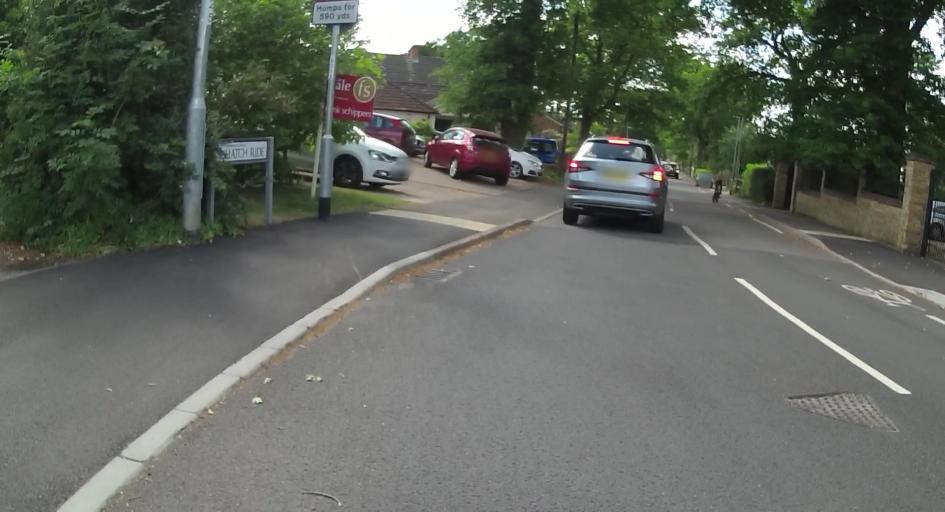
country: GB
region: England
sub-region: Bracknell Forest
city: Crowthorne
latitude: 51.3792
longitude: -0.7914
